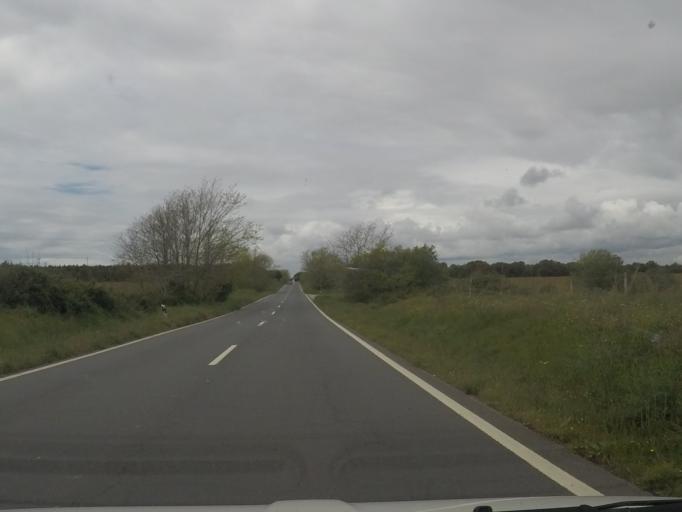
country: PT
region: Setubal
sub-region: Santiago do Cacem
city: Cercal
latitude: 37.8433
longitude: -8.7055
